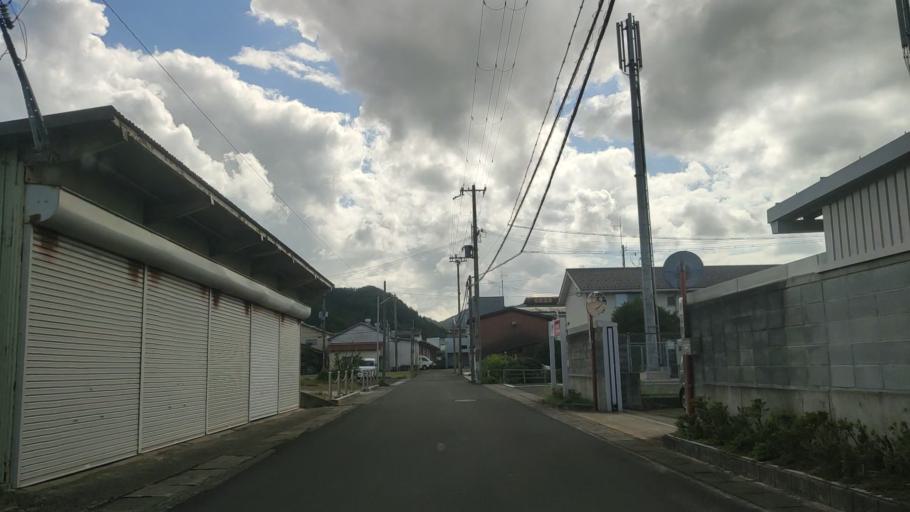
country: JP
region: Hyogo
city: Toyooka
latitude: 35.6043
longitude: 134.8961
